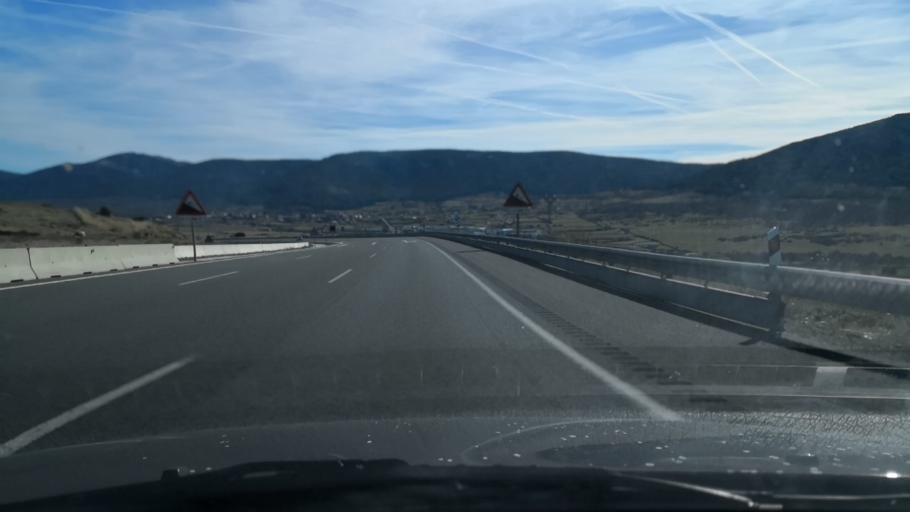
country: ES
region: Castille and Leon
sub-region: Provincia de Segovia
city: Vegas de Matute
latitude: 40.7412
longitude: -4.2749
